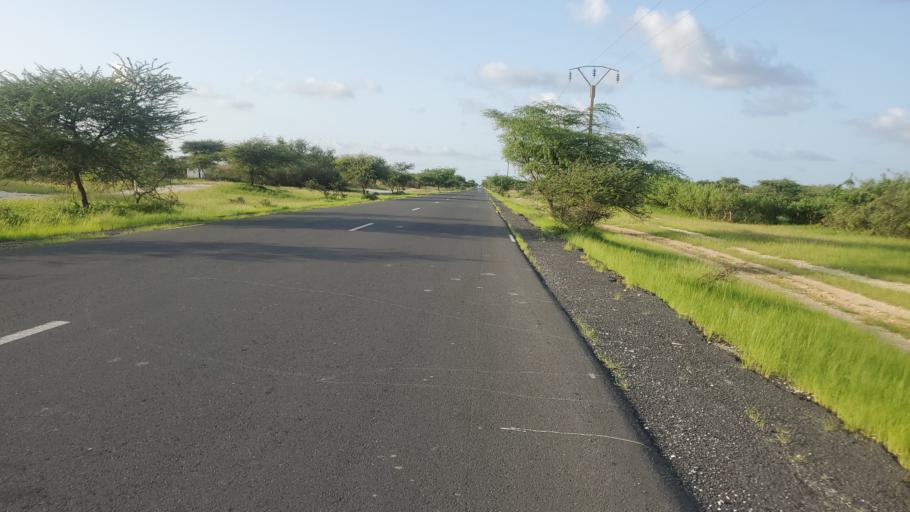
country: SN
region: Saint-Louis
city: Saint-Louis
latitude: 16.1670
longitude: -16.4099
